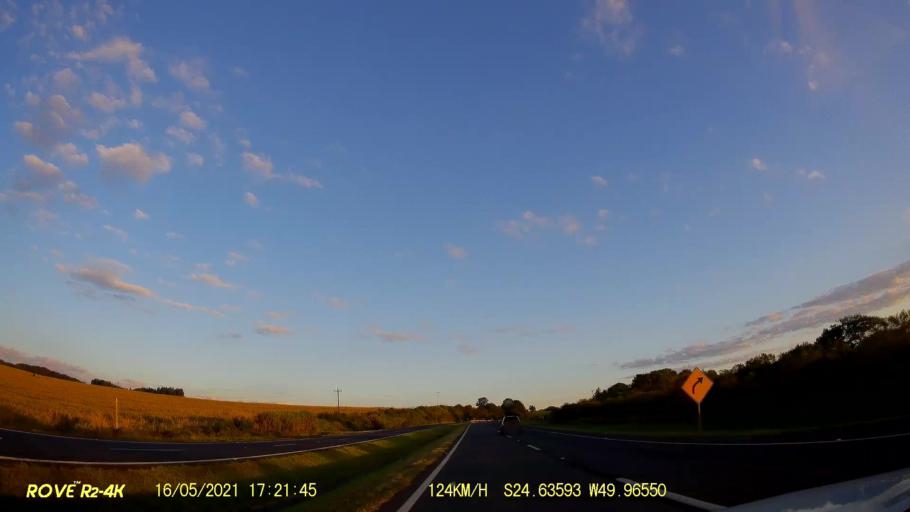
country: BR
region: Parana
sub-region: Pirai Do Sul
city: Pirai do Sul
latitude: -24.6363
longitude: -49.9655
